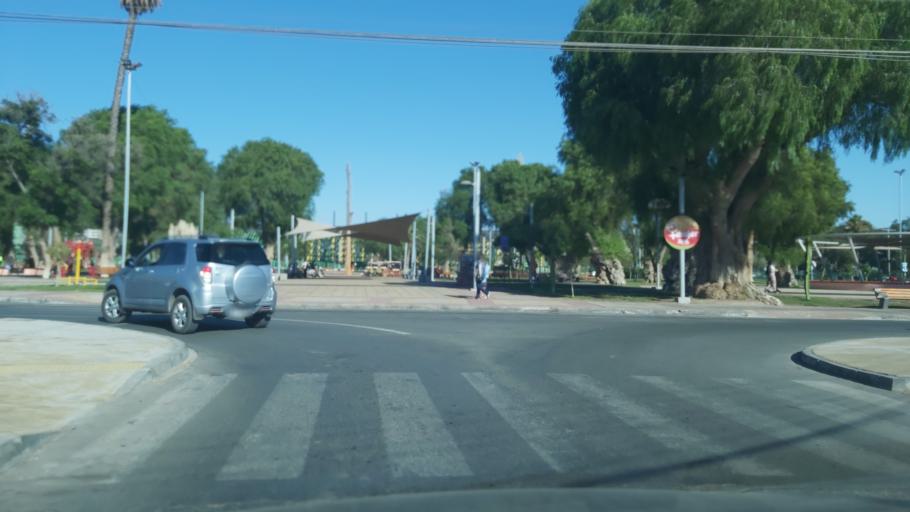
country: CL
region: Atacama
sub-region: Provincia de Copiapo
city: Copiapo
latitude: -27.3756
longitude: -70.3227
